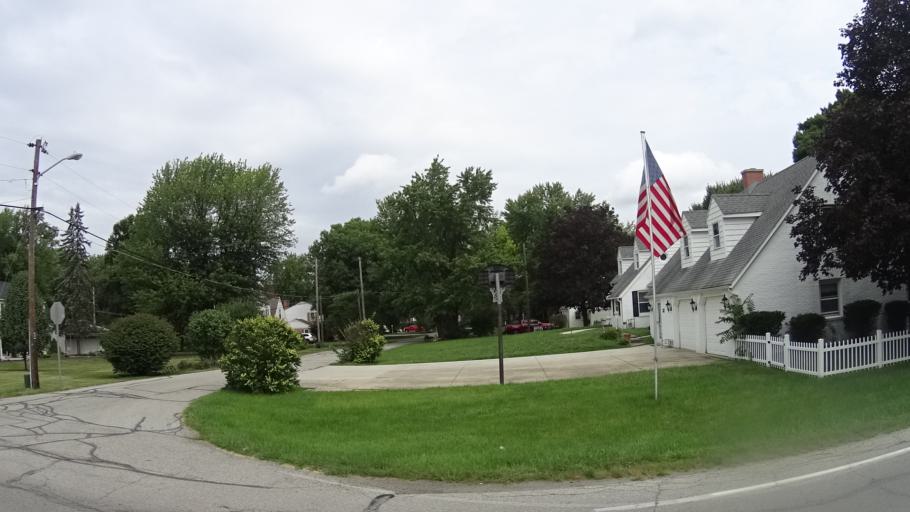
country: US
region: Indiana
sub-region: Madison County
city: Edgewood
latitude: 40.1014
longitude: -85.7347
